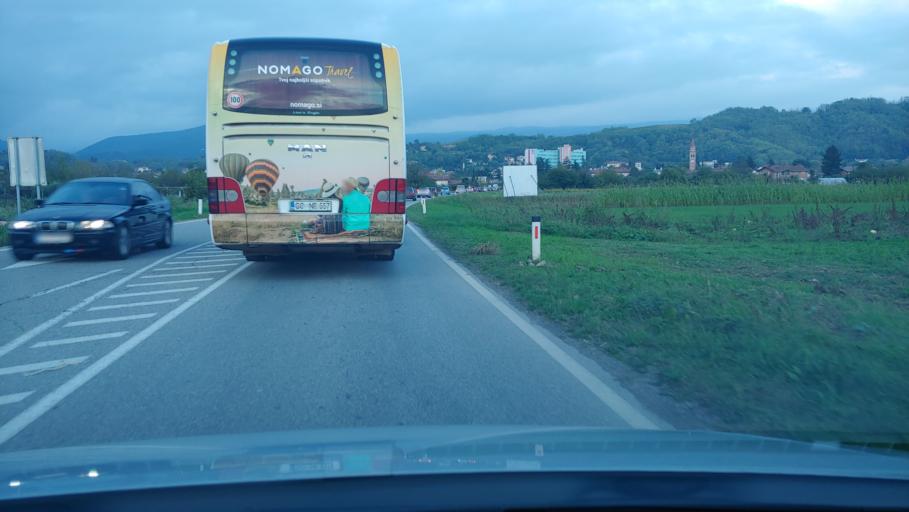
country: SI
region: Sempeter-Vrtojba
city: Sempeter pri Gorici
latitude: 45.9274
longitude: 13.6312
